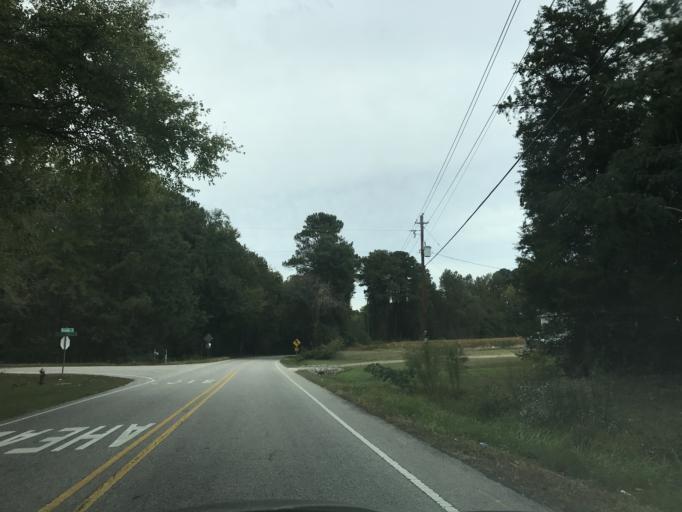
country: US
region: North Carolina
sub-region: Wake County
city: Knightdale
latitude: 35.8294
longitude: -78.5126
